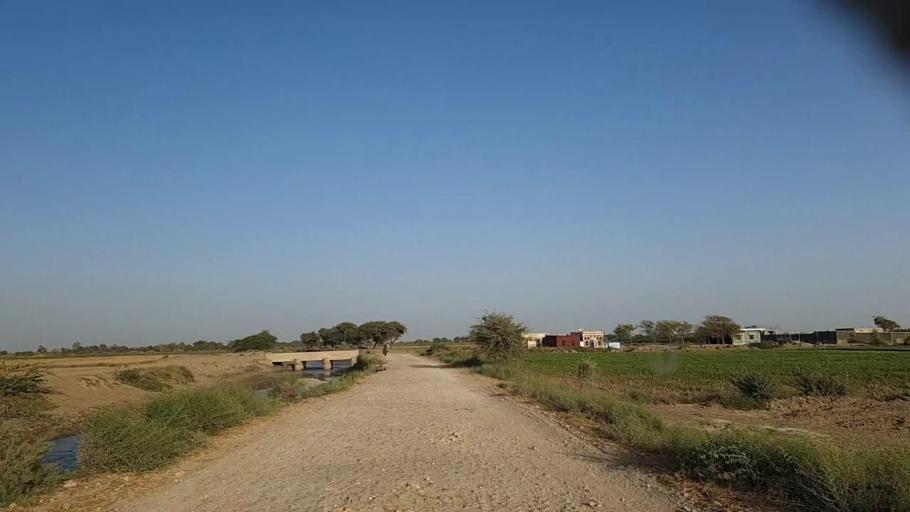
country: PK
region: Sindh
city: Jati
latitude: 24.4143
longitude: 68.3147
